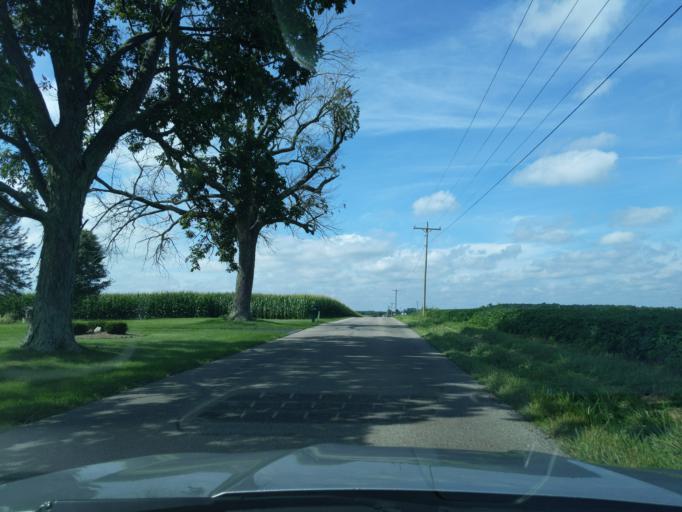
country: US
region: Indiana
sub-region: Ripley County
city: Batesville
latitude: 39.2855
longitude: -85.3477
